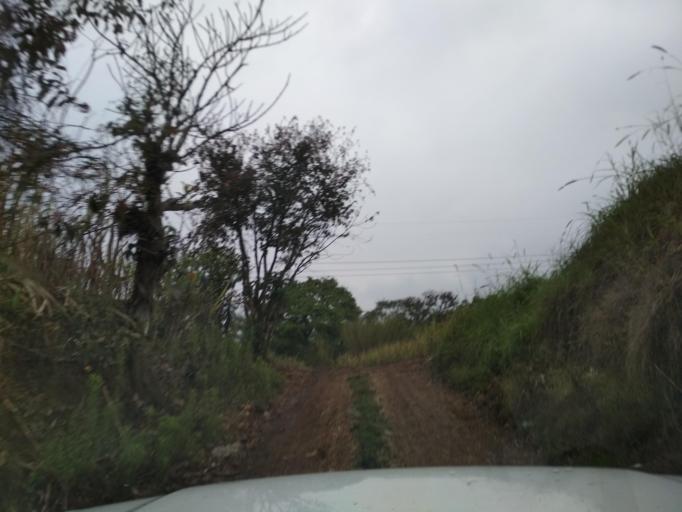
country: MX
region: Veracruz
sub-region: Cordoba
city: Fredepo
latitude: 18.8710
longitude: -96.9677
